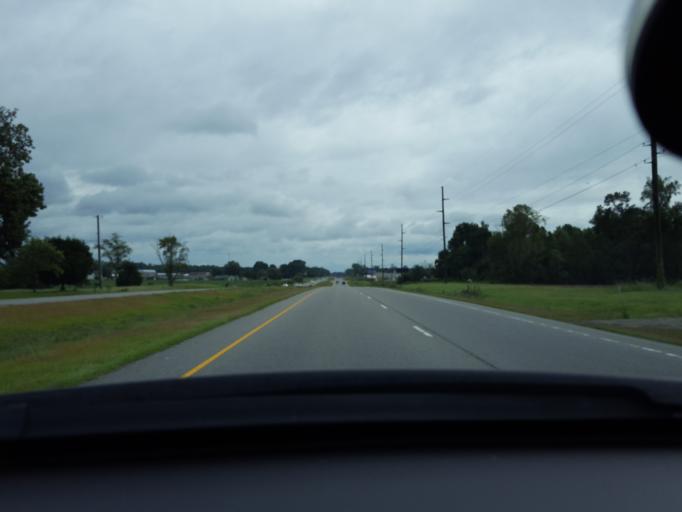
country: US
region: North Carolina
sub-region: Pitt County
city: Ayden
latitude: 35.4370
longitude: -77.4330
